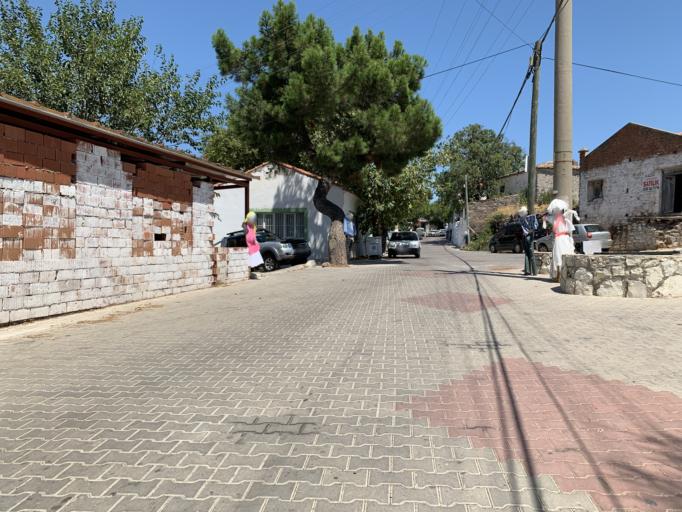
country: TR
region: Izmir
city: Uzunkuyu
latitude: 38.3229
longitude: 26.5792
